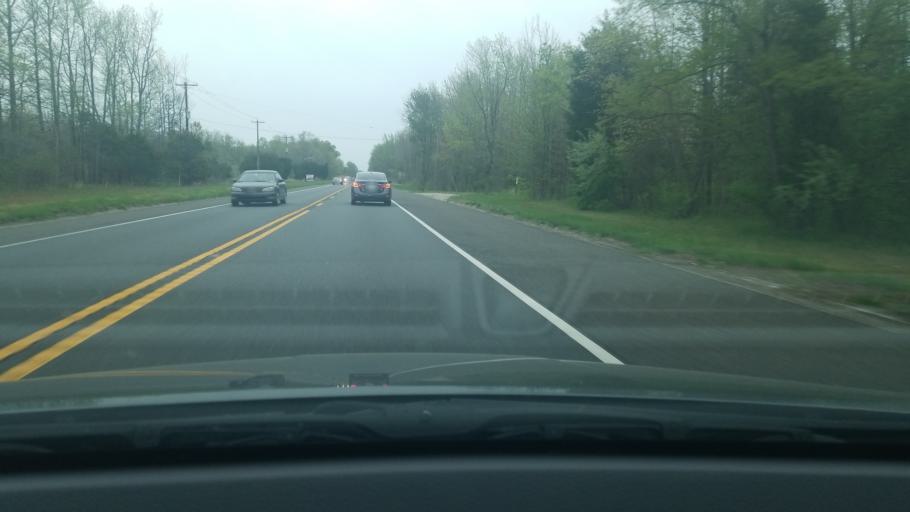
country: US
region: New Jersey
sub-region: Burlington County
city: Mount Laurel
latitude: 39.8958
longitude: -74.8724
